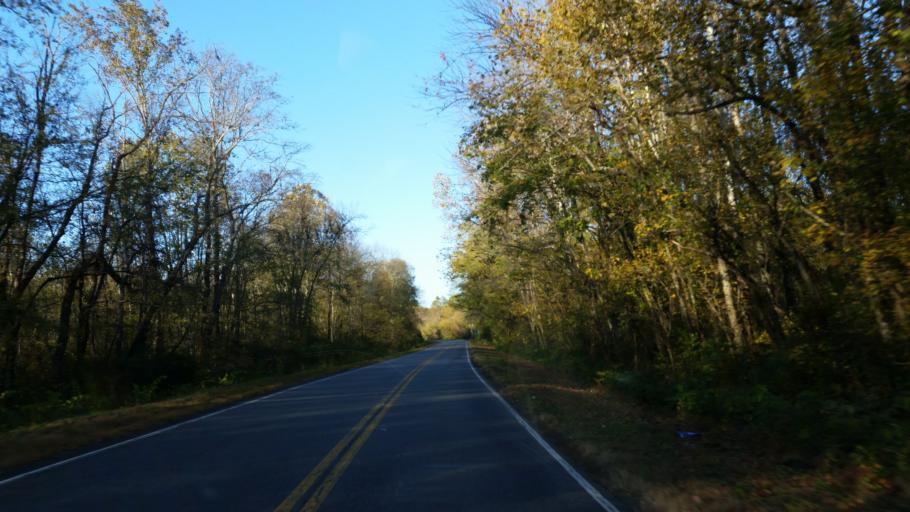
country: US
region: Georgia
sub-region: Bartow County
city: Adairsville
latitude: 34.2677
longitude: -84.9581
